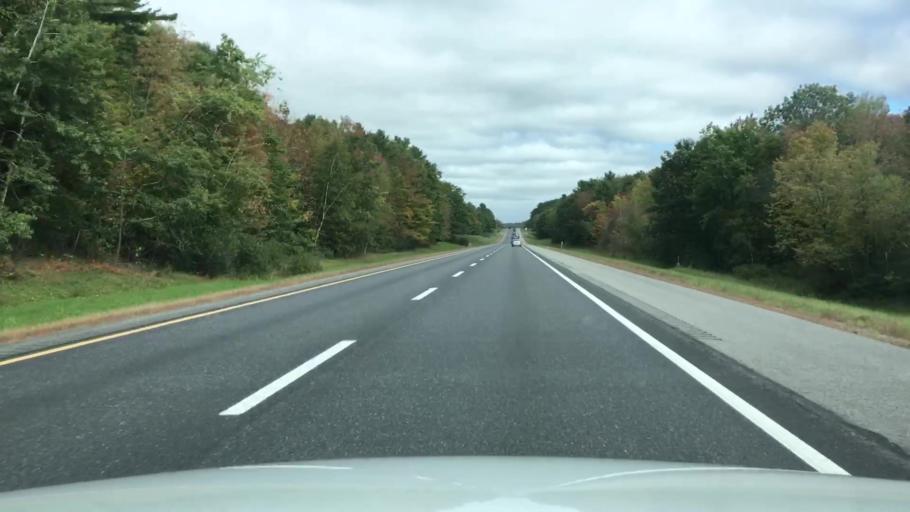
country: US
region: Maine
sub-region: Sagadahoc County
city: Topsham
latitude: 44.0312
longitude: -69.9098
